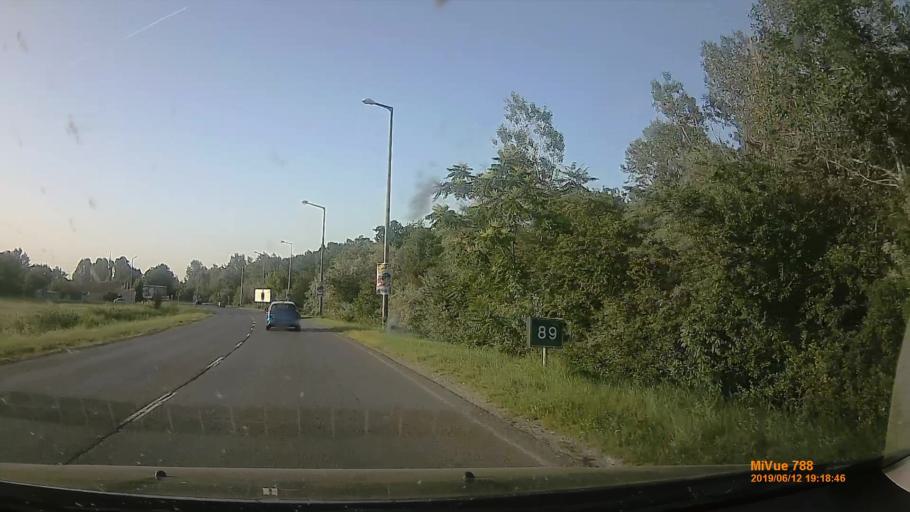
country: HU
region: Bacs-Kiskun
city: Kecskemet
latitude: 46.8928
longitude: 19.7059
